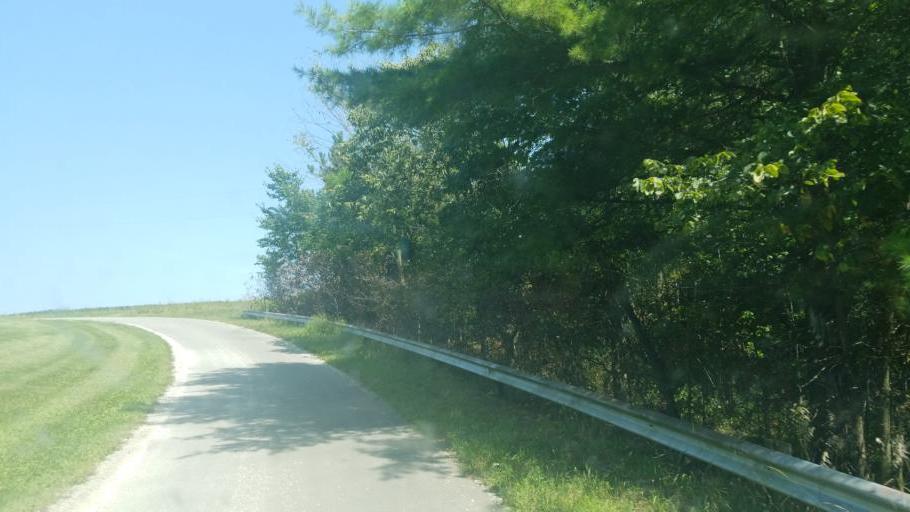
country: US
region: Ohio
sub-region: Crawford County
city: Bucyrus
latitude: 40.9346
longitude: -83.0602
